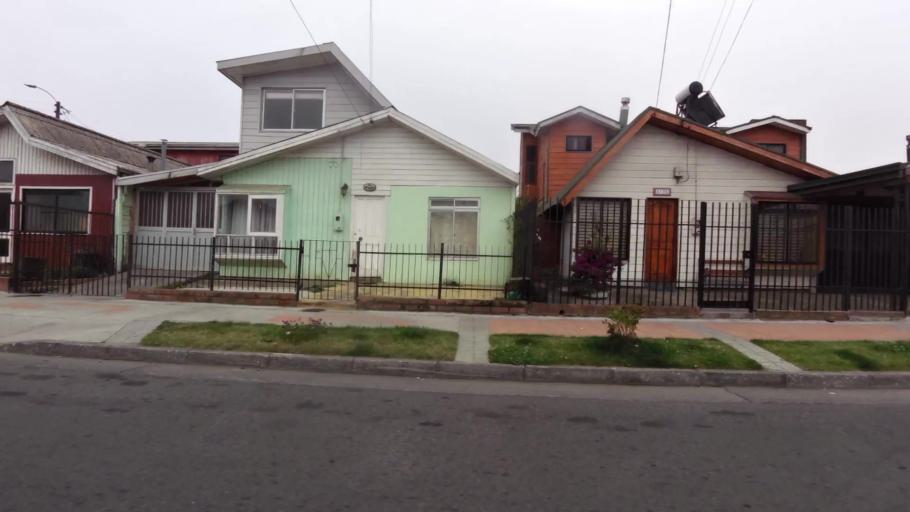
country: CL
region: Biobio
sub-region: Provincia de Concepcion
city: Concepcion
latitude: -36.7942
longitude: -73.0812
